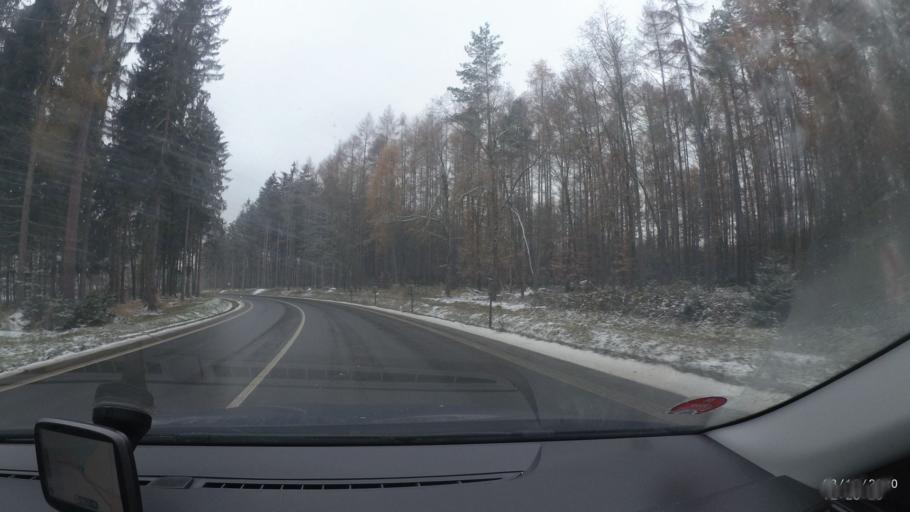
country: CZ
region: Central Bohemia
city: Nove Straseci
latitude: 50.1654
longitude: 13.8818
